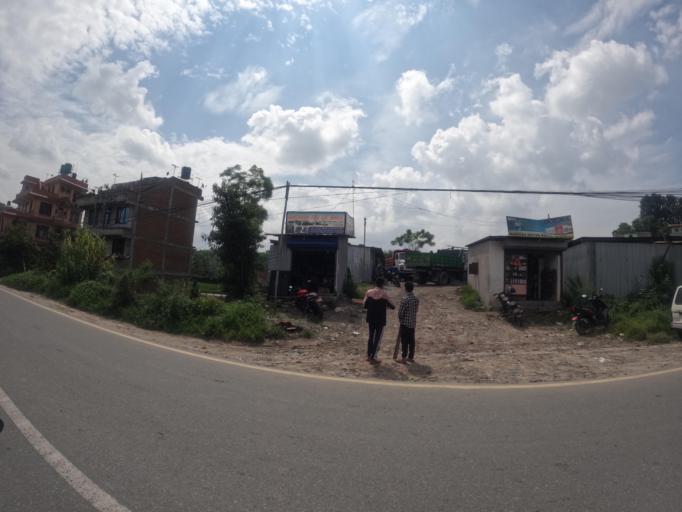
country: NP
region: Central Region
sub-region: Bagmati Zone
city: Bhaktapur
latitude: 27.6822
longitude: 85.3815
